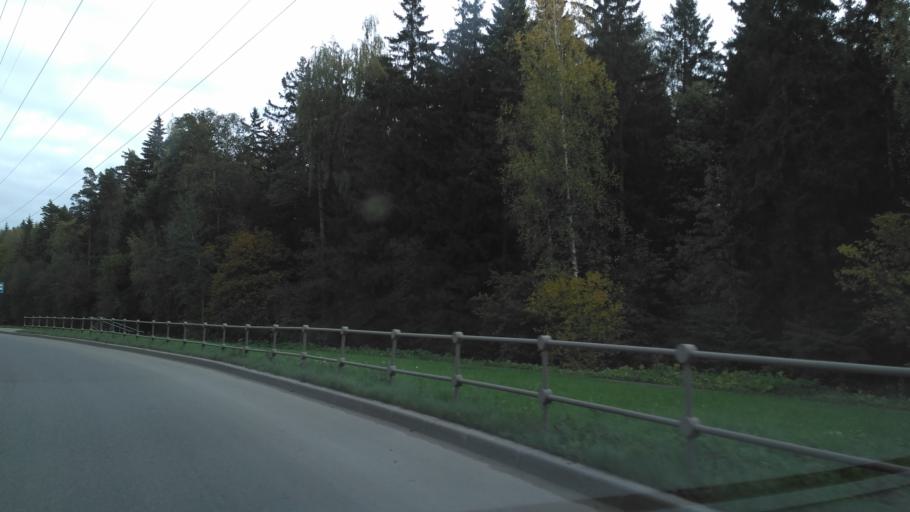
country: RU
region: Moskovskaya
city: Alabushevo
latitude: 56.0072
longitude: 37.1716
